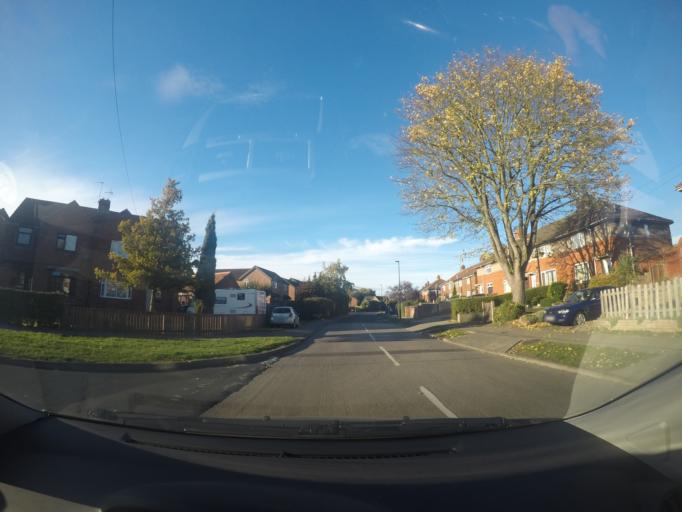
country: GB
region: England
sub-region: City of York
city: York
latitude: 53.9730
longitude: -1.0966
